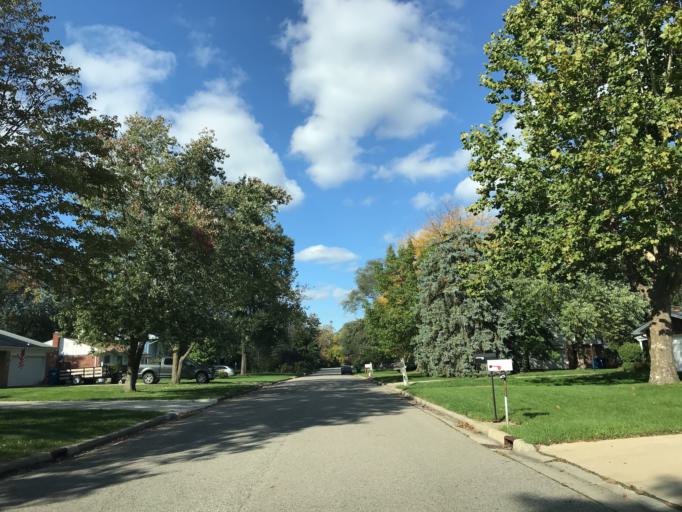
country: US
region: Michigan
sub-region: Washtenaw County
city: Ypsilanti
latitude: 42.2472
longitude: -83.6717
